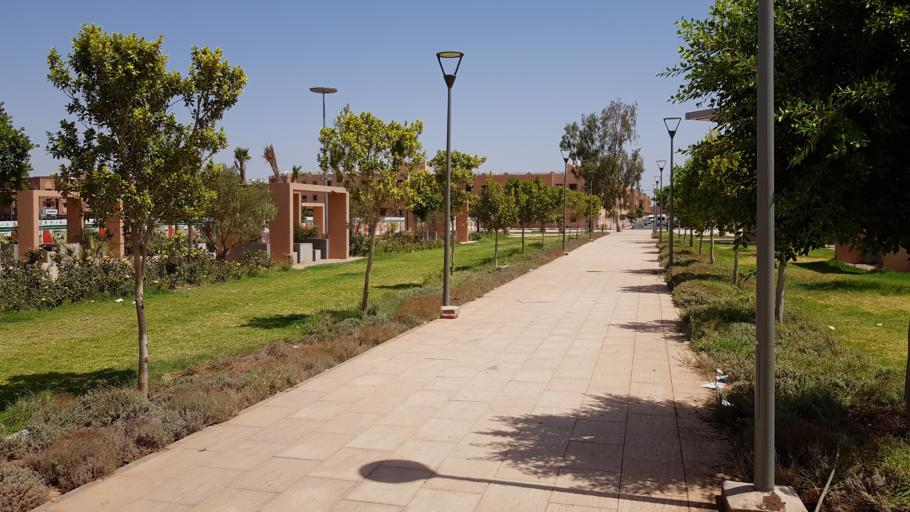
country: MA
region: Marrakech-Tensift-Al Haouz
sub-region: Marrakech
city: Marrakesh
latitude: 31.5925
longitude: -8.0295
